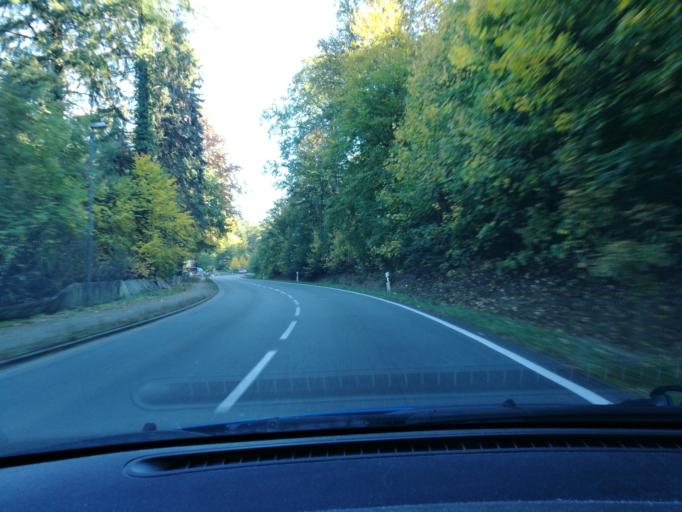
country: DE
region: Lower Saxony
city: Gohrde
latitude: 53.1385
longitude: 10.8800
